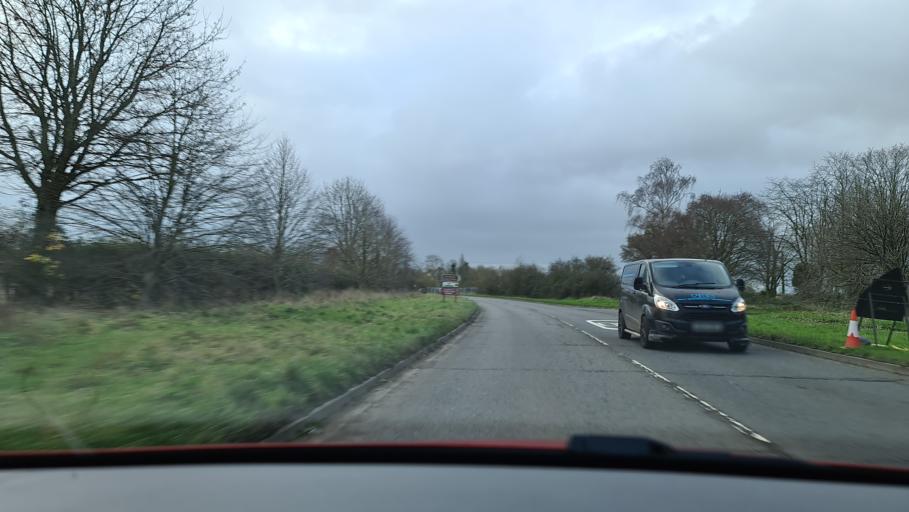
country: GB
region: England
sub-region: Buckinghamshire
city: Weston Turville
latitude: 51.7778
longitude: -0.7911
